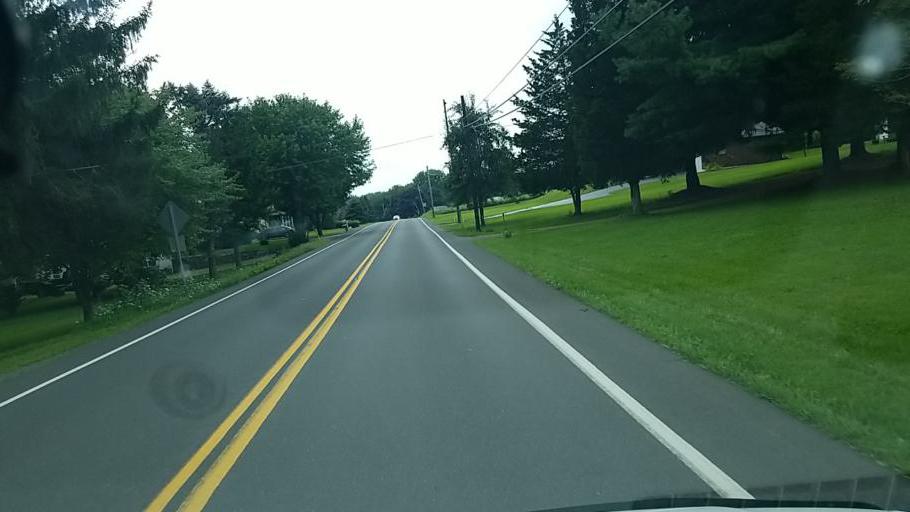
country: US
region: Pennsylvania
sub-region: Dauphin County
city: Elizabethville
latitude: 40.5146
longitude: -76.8637
